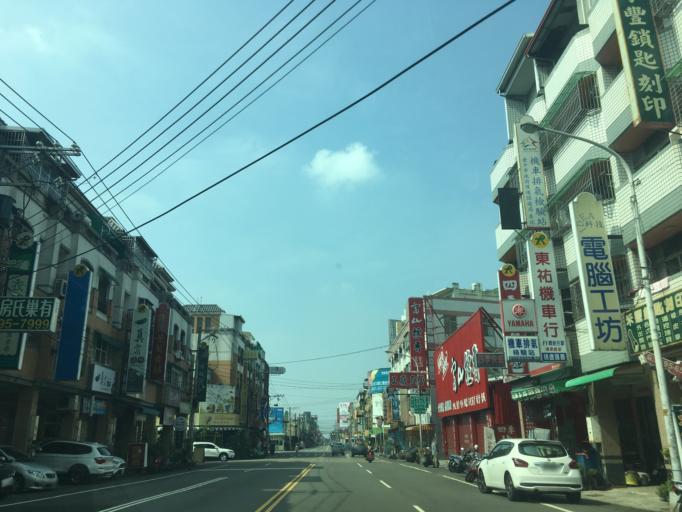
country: TW
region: Taiwan
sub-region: Taichung City
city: Taichung
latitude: 24.1523
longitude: 120.7112
